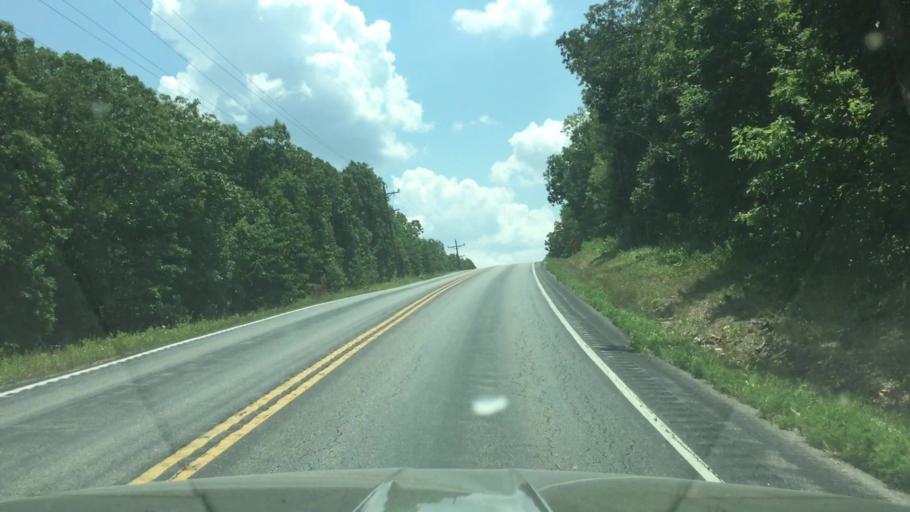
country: US
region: Missouri
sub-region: Camden County
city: Osage Beach
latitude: 38.1333
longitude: -92.5612
